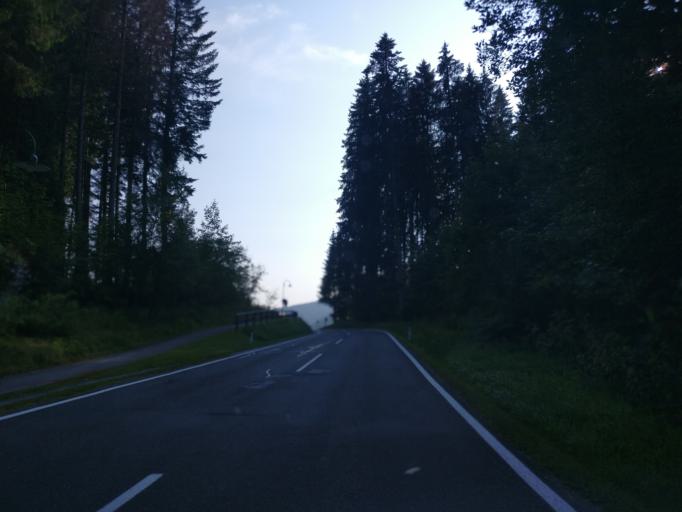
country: AT
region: Salzburg
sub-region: Politischer Bezirk Sankt Johann im Pongau
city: Werfenweng
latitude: 47.4569
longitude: 13.2483
